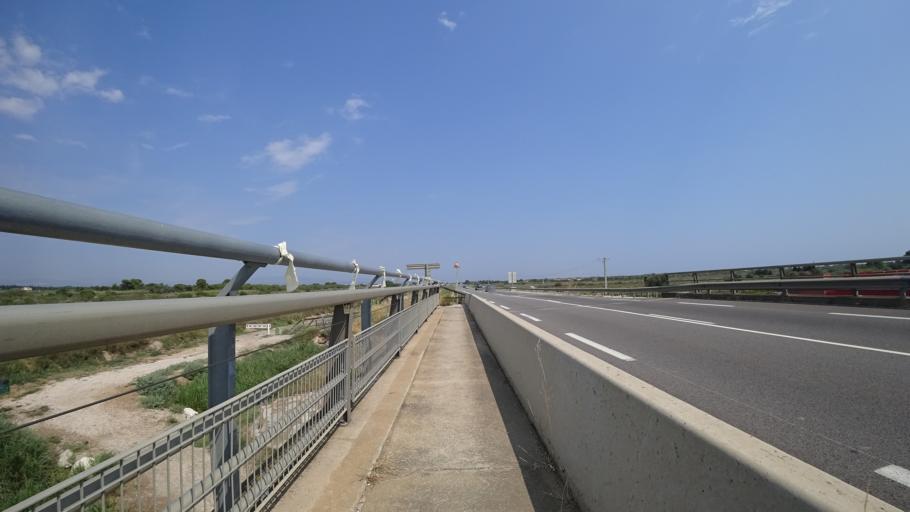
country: FR
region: Languedoc-Roussillon
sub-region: Departement des Pyrenees-Orientales
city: Torreilles
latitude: 42.7525
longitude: 3.0213
